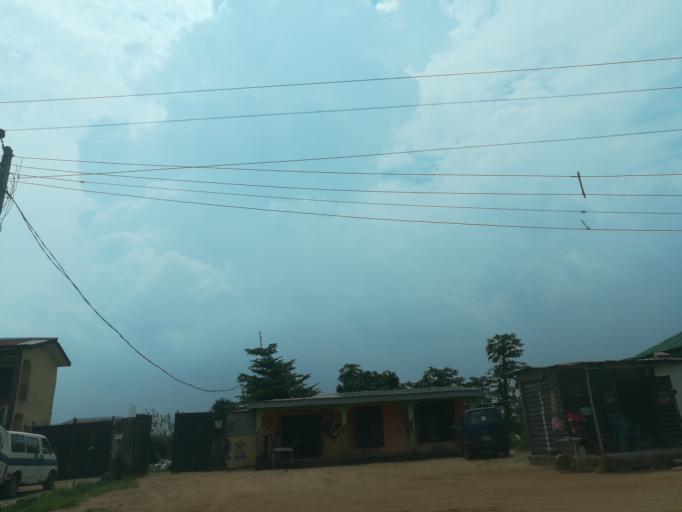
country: NG
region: Lagos
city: Ikorodu
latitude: 6.5929
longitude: 3.5886
